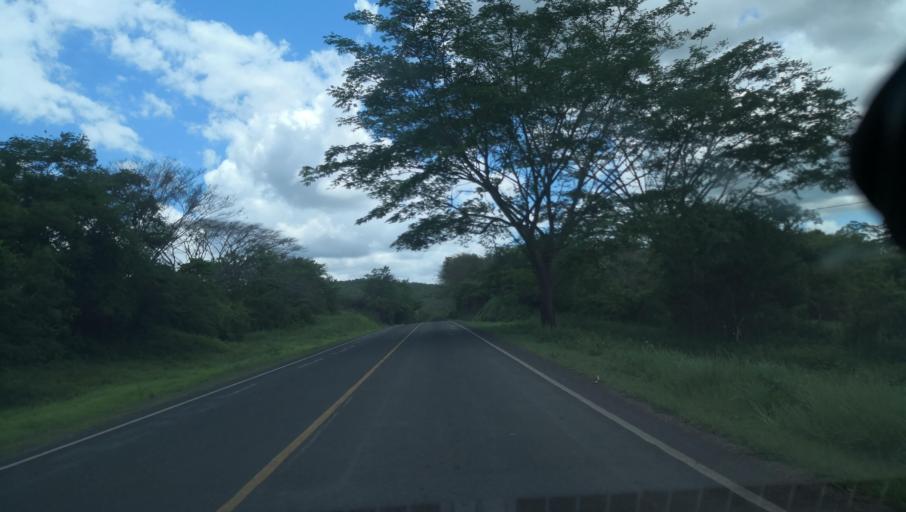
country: NI
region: Madriz
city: Palacaguina
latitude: 13.4344
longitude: -86.4171
